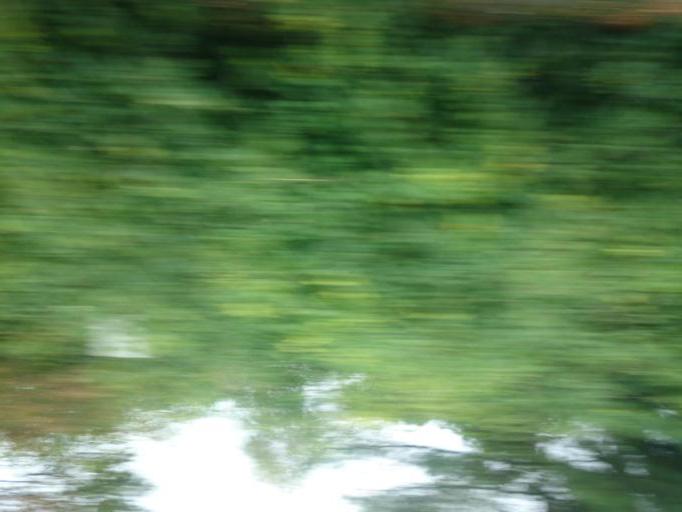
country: DE
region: Saxony-Anhalt
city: Dieskau
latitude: 51.4462
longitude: 12.0266
